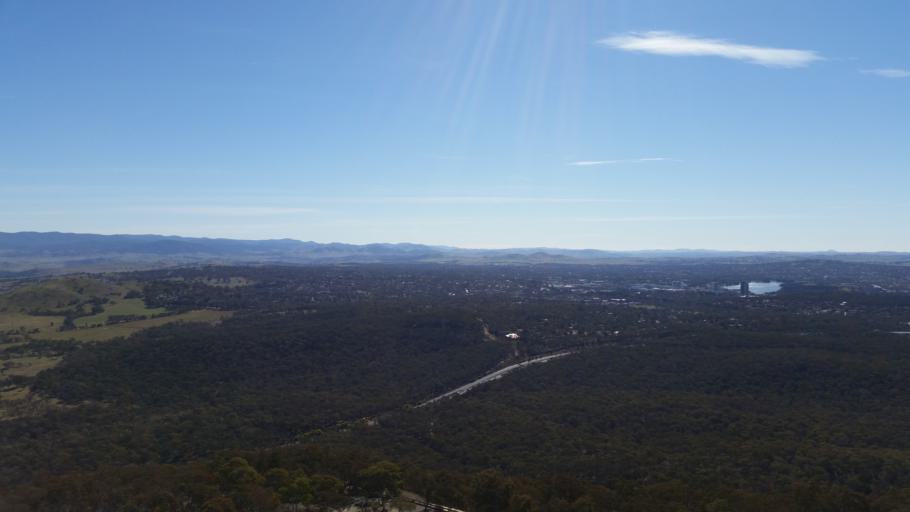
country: AU
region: Australian Capital Territory
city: Acton
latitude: -35.2755
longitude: 149.0978
